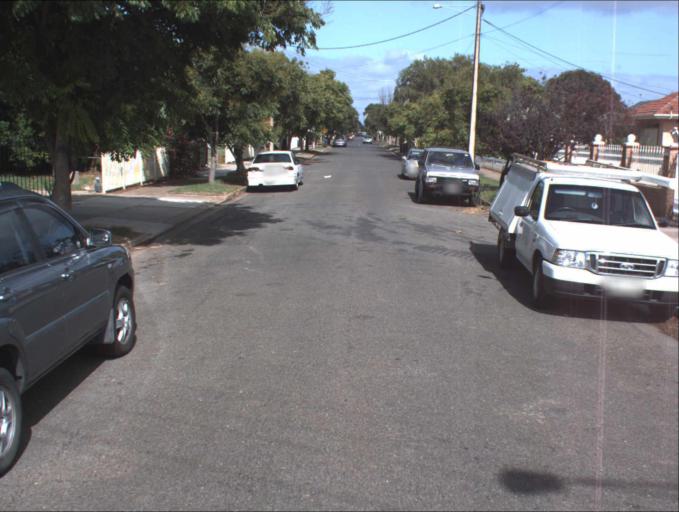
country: AU
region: South Australia
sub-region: Charles Sturt
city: Woodville North
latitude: -34.8712
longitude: 138.5536
